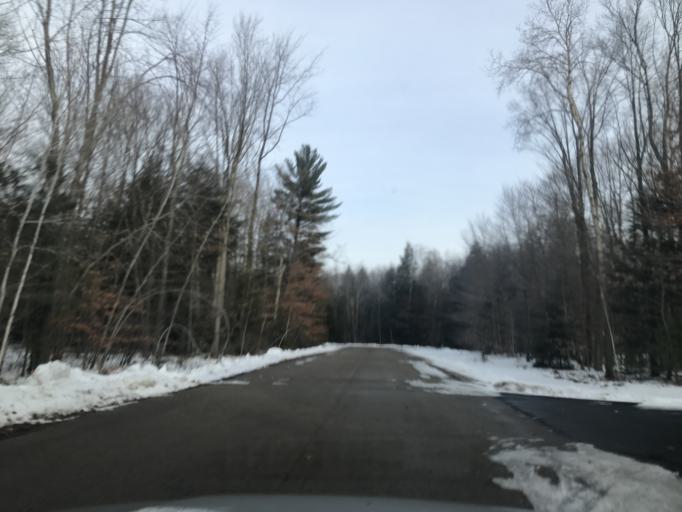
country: US
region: Wisconsin
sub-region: Brown County
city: Suamico
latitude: 44.6906
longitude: -88.0615
